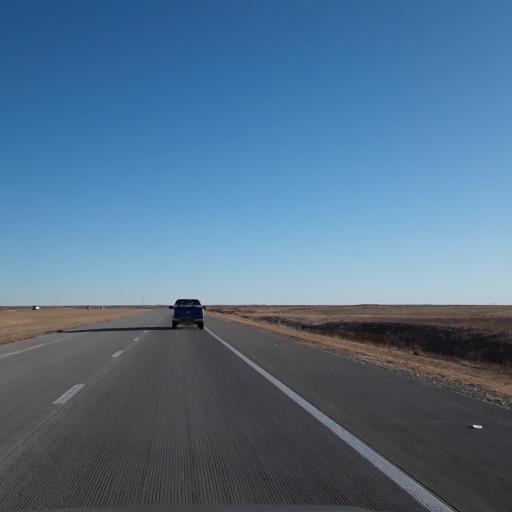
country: US
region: Kansas
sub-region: Seward County
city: Liberal
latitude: 37.1067
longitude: -100.7894
